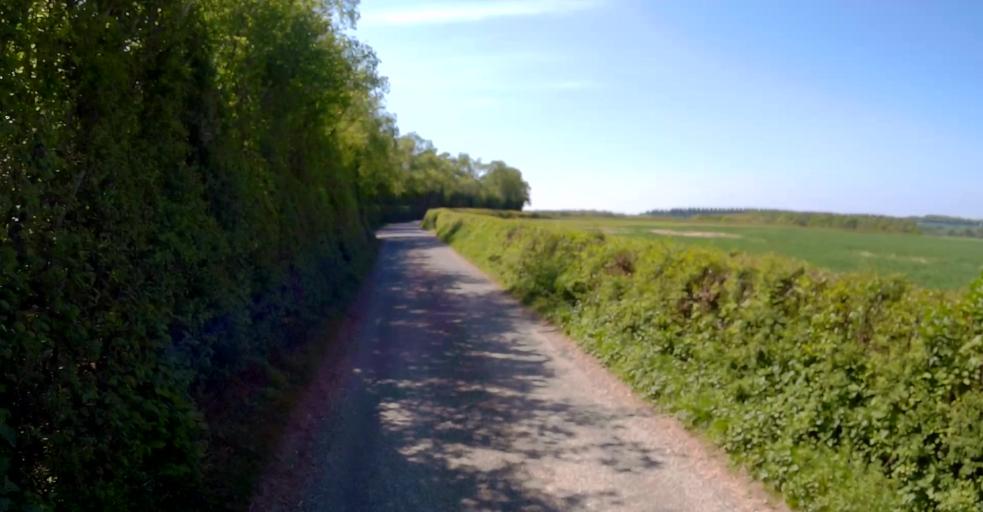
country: GB
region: England
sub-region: Hampshire
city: Overton
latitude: 51.2029
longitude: -1.2406
